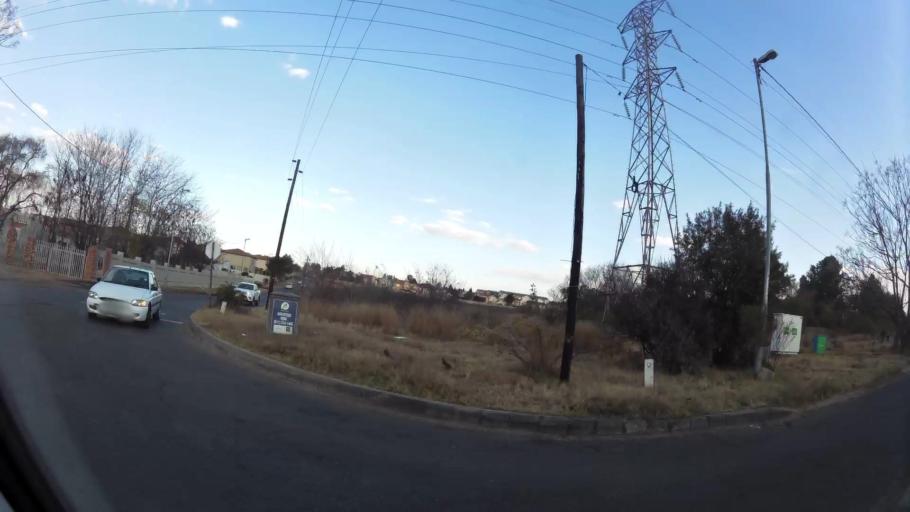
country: ZA
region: Gauteng
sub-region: City of Johannesburg Metropolitan Municipality
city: Diepsloot
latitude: -25.9945
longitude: 27.9989
